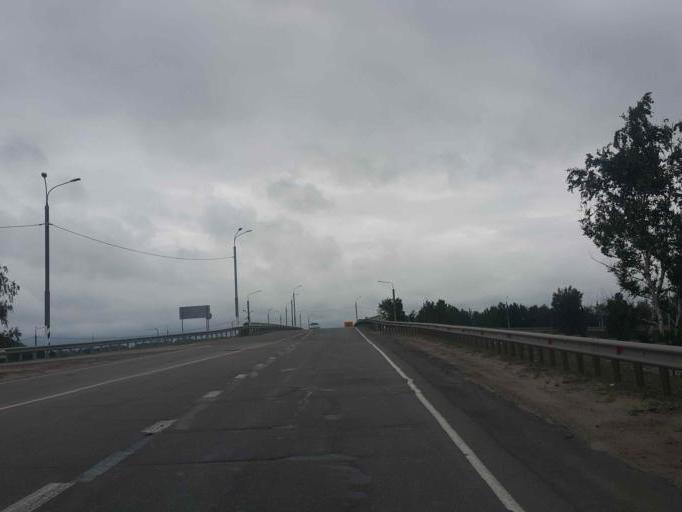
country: RU
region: Tambov
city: Komsomolets
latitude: 52.7325
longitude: 41.2963
